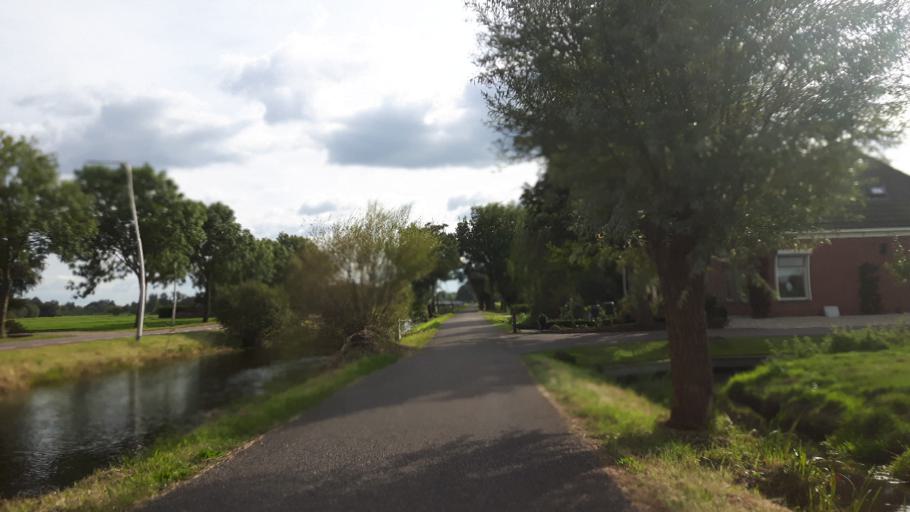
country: NL
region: Utrecht
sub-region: Gemeente Woerden
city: Woerden
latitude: 52.1046
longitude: 4.8942
